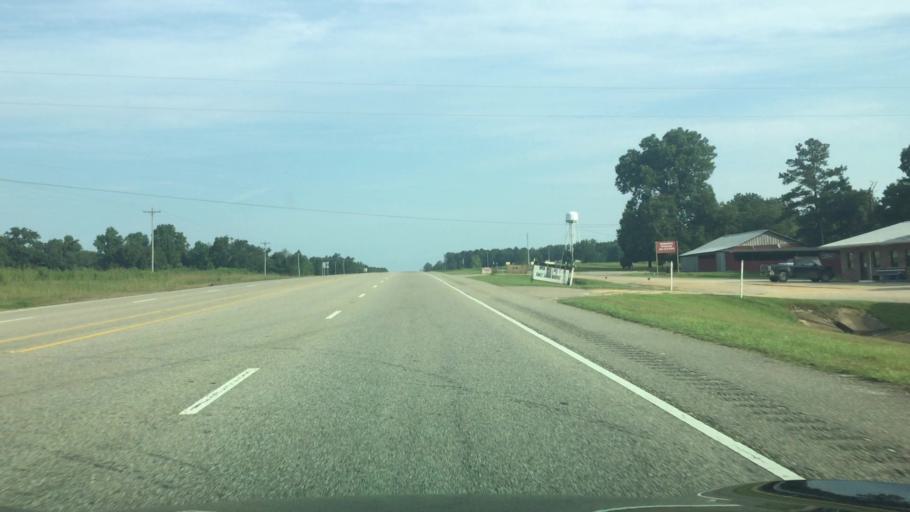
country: US
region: Alabama
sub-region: Butler County
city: Georgiana
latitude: 31.5264
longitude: -86.7179
